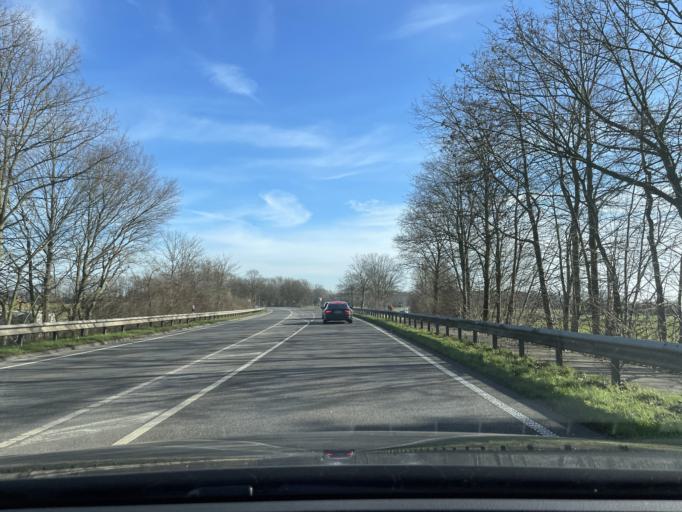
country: DE
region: North Rhine-Westphalia
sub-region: Regierungsbezirk Dusseldorf
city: Korschenbroich
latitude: 51.2193
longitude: 6.5071
